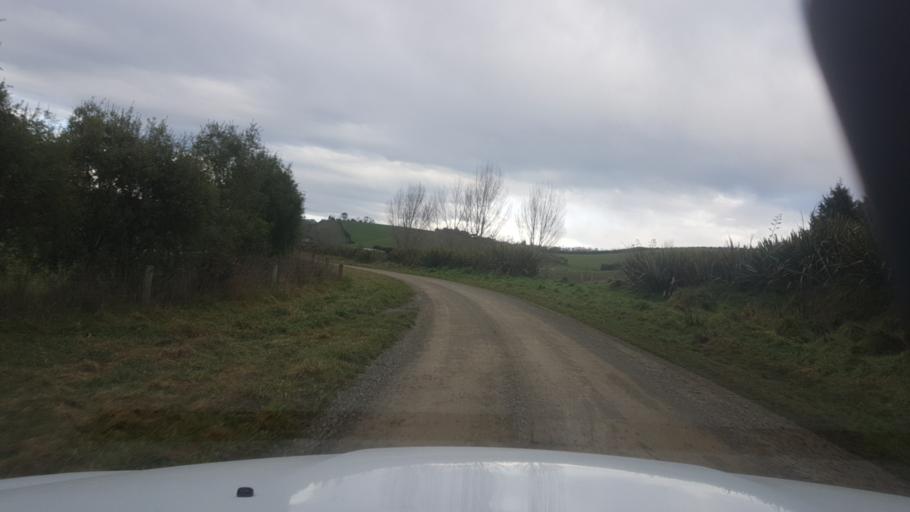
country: NZ
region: Canterbury
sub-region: Timaru District
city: Pleasant Point
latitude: -44.3421
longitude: 171.1618
